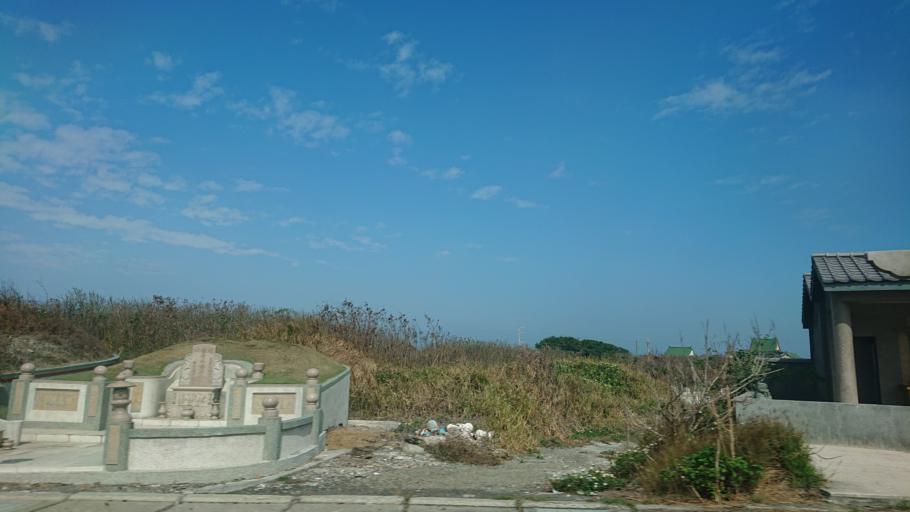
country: TW
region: Taiwan
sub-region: Changhua
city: Chang-hua
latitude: 23.9194
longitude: 120.3162
